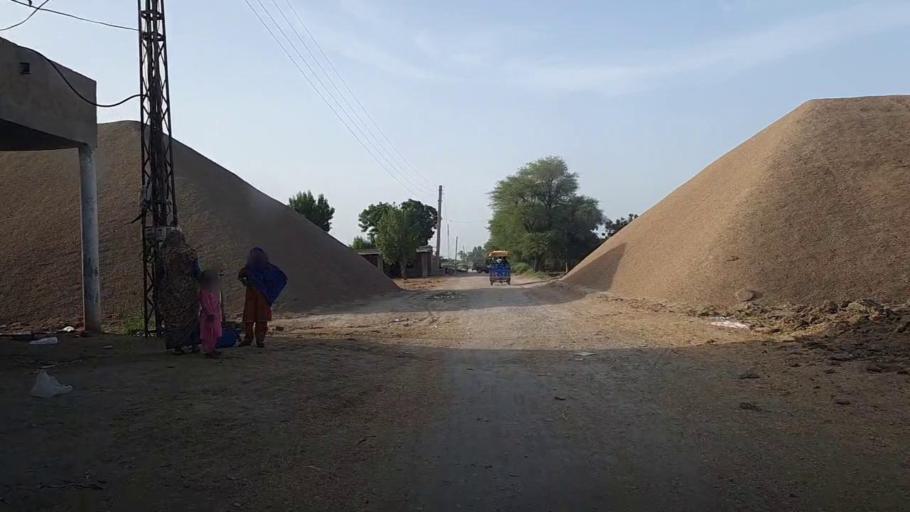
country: PK
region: Sindh
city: Bhiria
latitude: 26.8907
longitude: 68.2619
